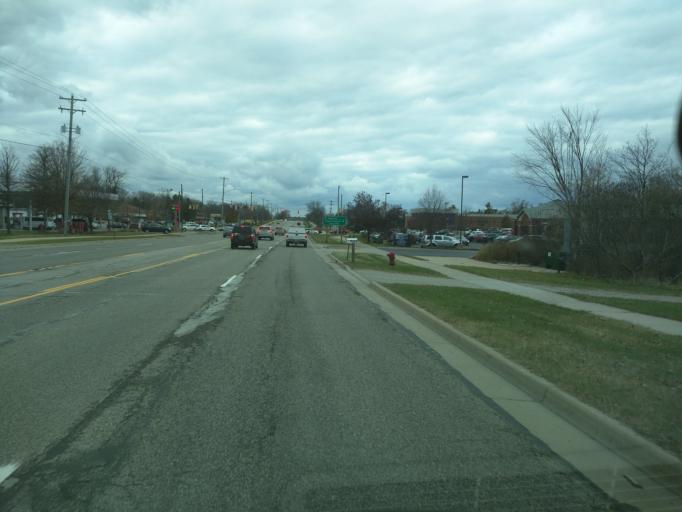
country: US
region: Michigan
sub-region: Ingham County
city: Okemos
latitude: 42.7174
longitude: -84.4081
